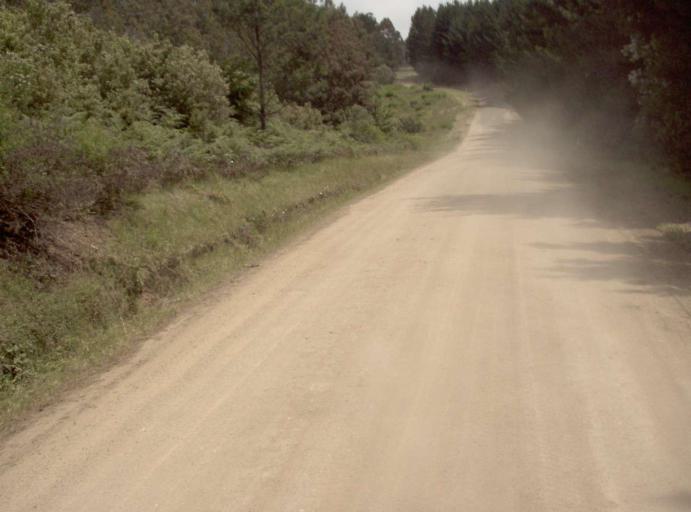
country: AU
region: Victoria
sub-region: Latrobe
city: Traralgon
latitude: -38.4128
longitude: 146.6194
